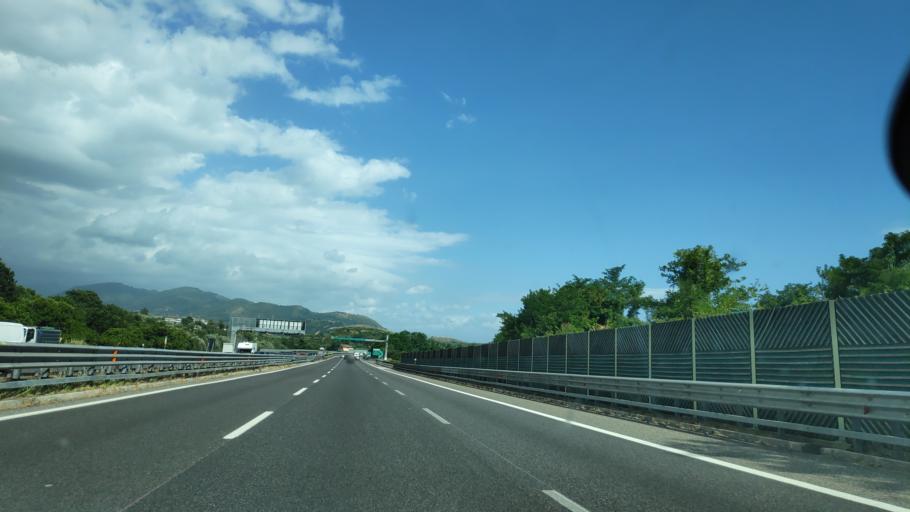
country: IT
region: Campania
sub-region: Provincia di Salerno
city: San Mango Piemonte
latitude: 40.6872
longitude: 14.8452
